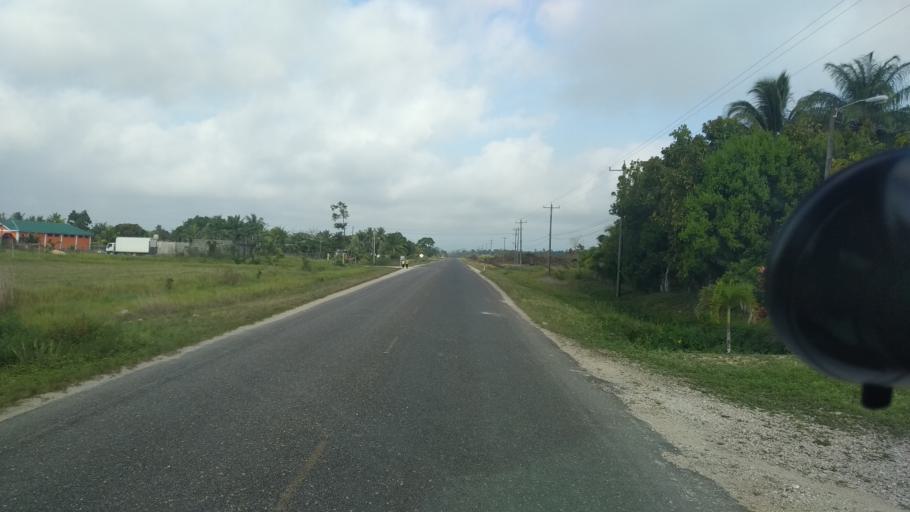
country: BZ
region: Stann Creek
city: Placencia
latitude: 16.5123
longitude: -88.5423
